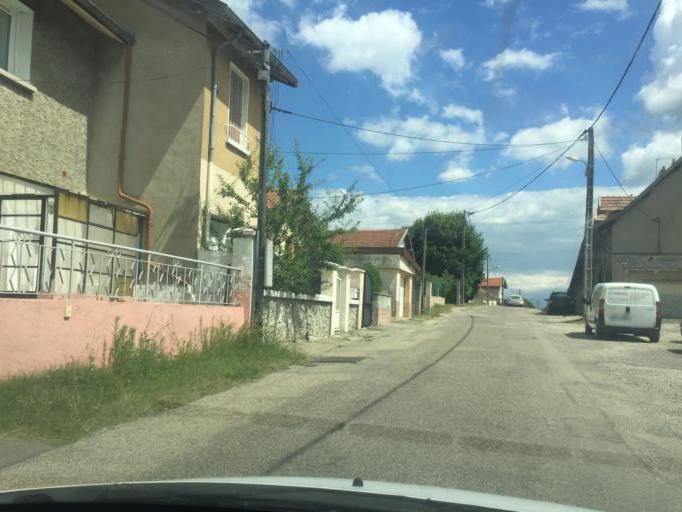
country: FR
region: Rhone-Alpes
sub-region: Departement de l'Isere
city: Charvieu-Chavagneux
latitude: 45.7539
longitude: 5.1614
